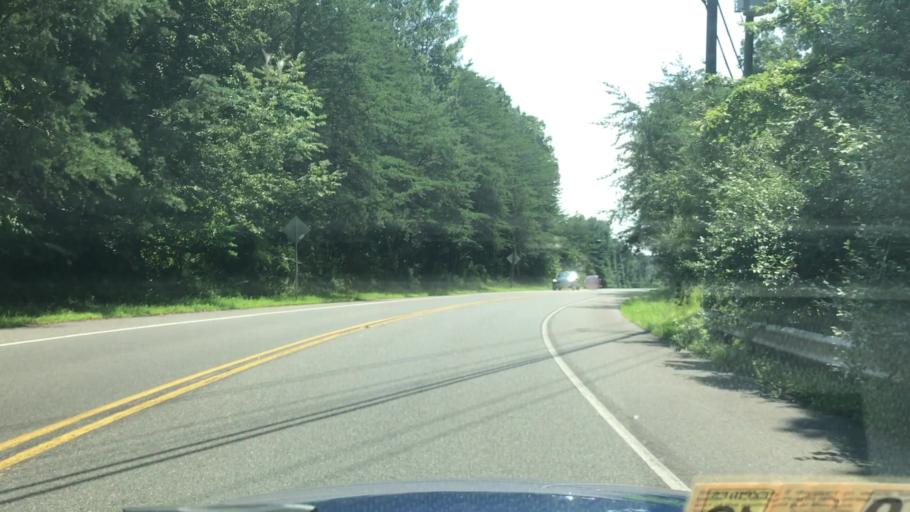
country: US
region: Virginia
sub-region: Fairfax County
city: Wolf Trap
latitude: 38.9272
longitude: -77.3226
